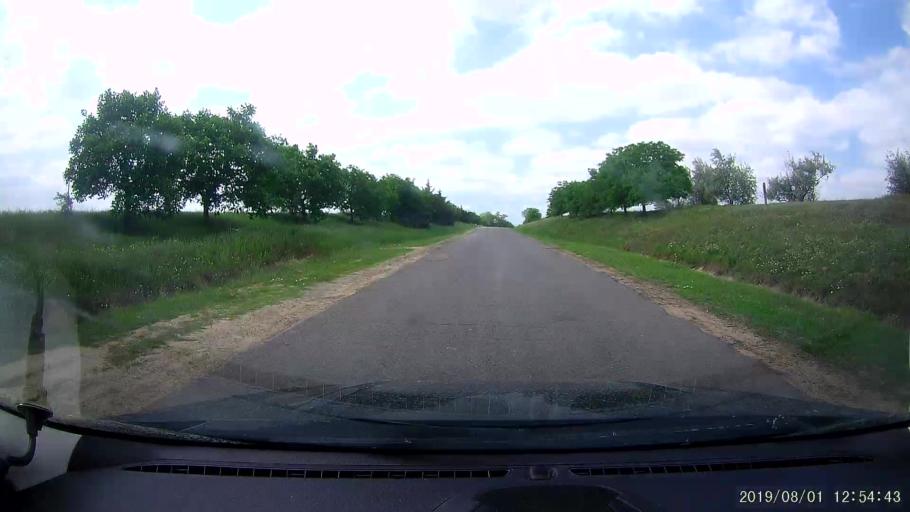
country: MD
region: Gagauzia
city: Vulcanesti
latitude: 45.6951
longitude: 28.4819
